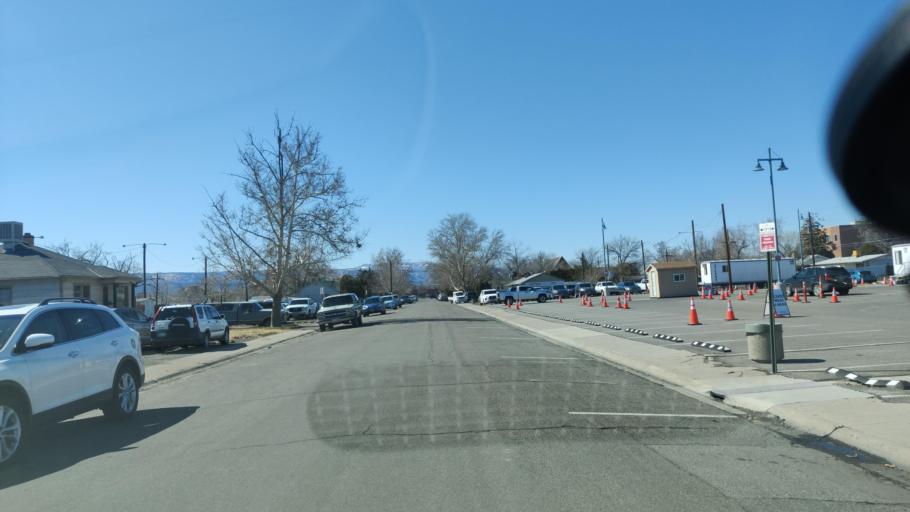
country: US
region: Colorado
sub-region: Mesa County
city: Grand Junction
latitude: 39.0782
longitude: -108.5570
